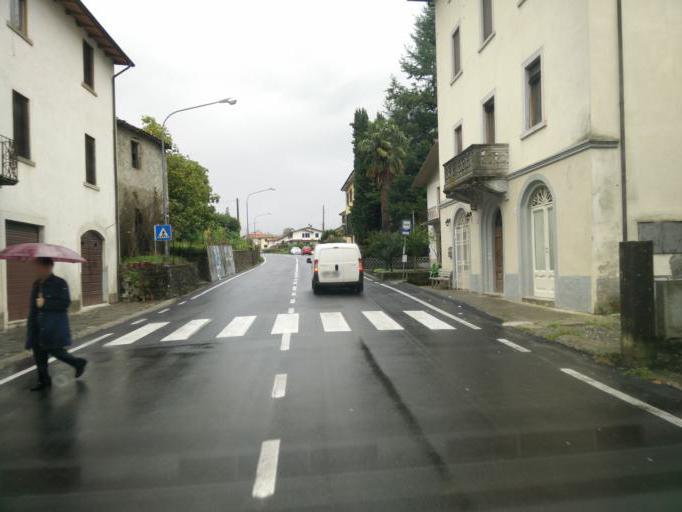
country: IT
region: Tuscany
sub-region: Provincia di Lucca
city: Barga
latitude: 44.0838
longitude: 10.4576
